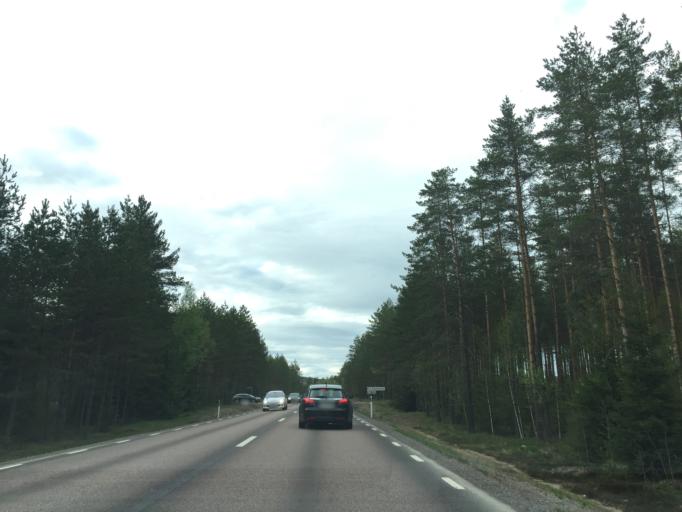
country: SE
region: Vaermland
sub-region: Eda Kommun
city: Charlottenberg
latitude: 59.9109
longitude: 12.2748
